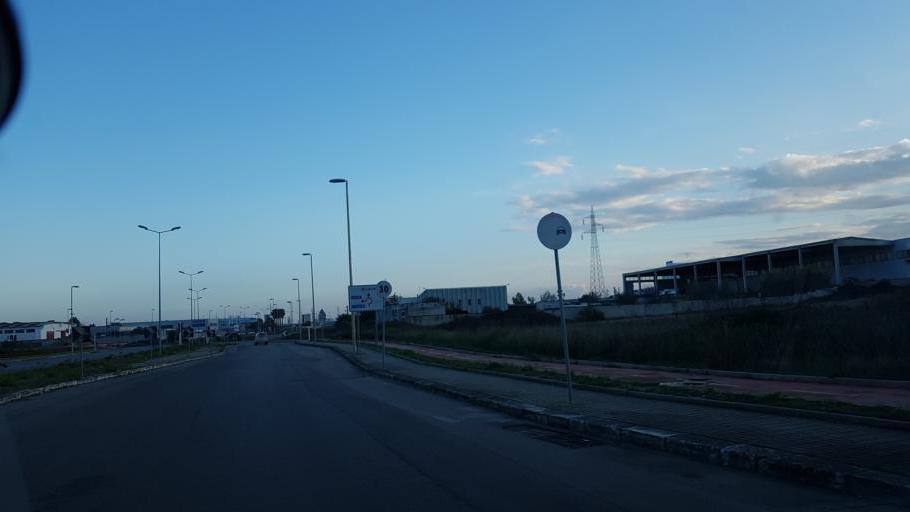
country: IT
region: Apulia
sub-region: Provincia di Lecce
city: Giorgilorio
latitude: 40.3751
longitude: 18.1341
